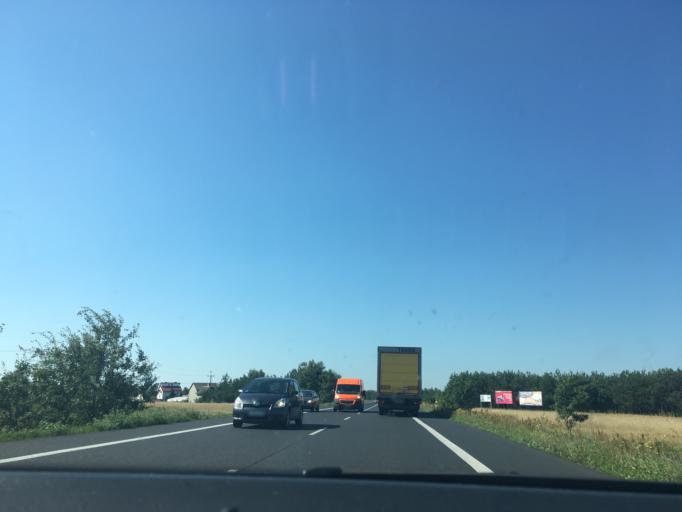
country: PL
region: Lublin Voivodeship
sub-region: Powiat lubartowski
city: Lubartow
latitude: 51.4710
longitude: 22.5833
